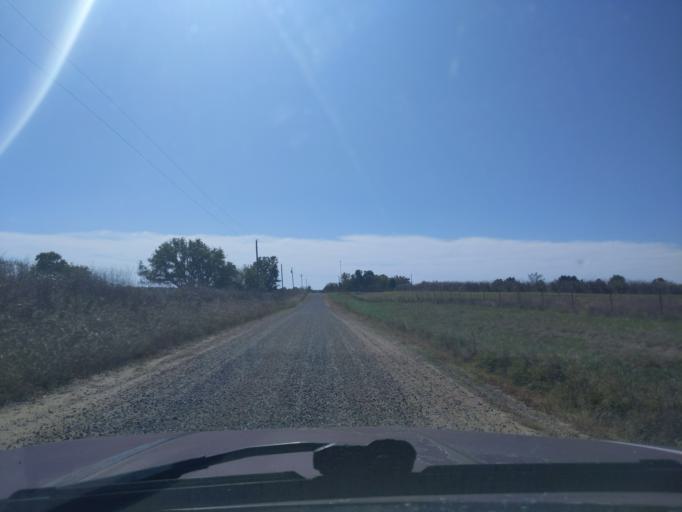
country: US
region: Oklahoma
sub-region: Okfuskee County
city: Boley
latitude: 35.6493
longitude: -96.4235
